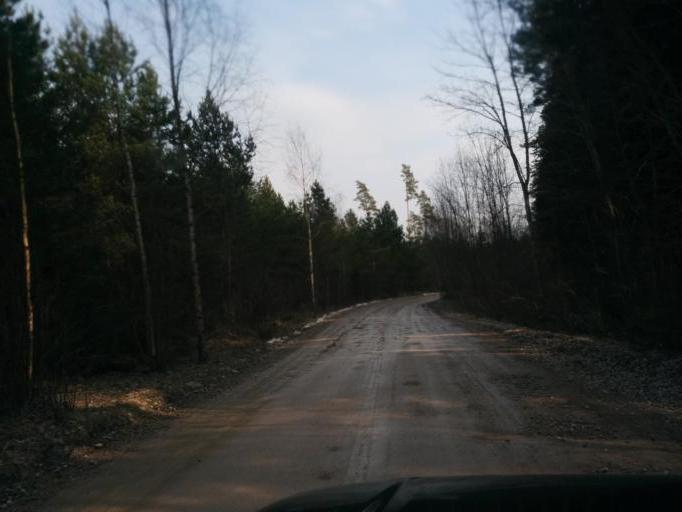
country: LV
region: Olaine
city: Olaine
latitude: 56.7896
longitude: 24.0415
